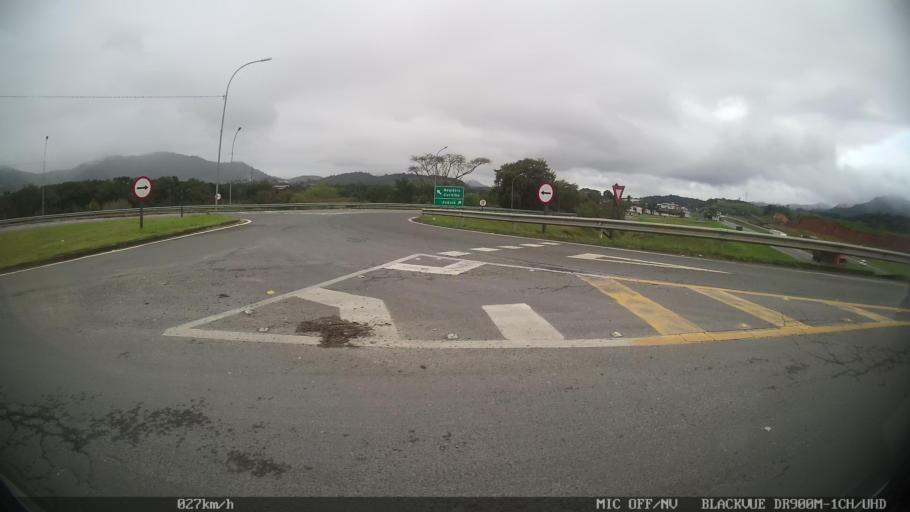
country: BR
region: Sao Paulo
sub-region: Juquia
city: Juquia
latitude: -24.3312
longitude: -47.6358
